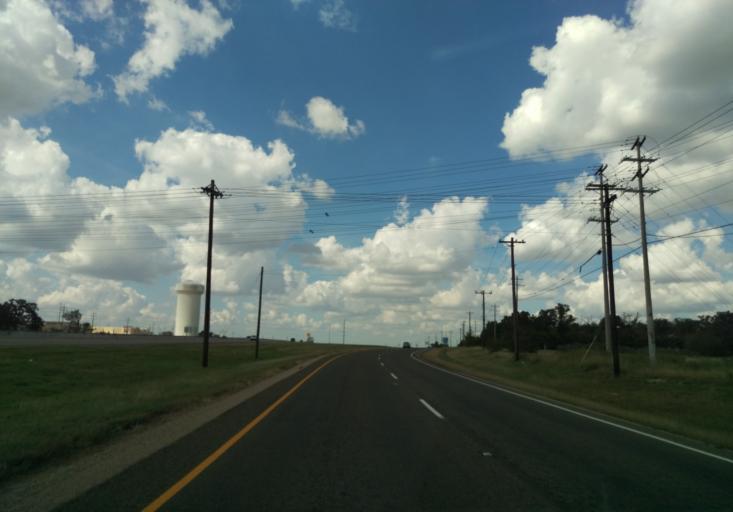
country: US
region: Texas
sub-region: Brazos County
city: College Station
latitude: 30.5561
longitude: -96.2534
